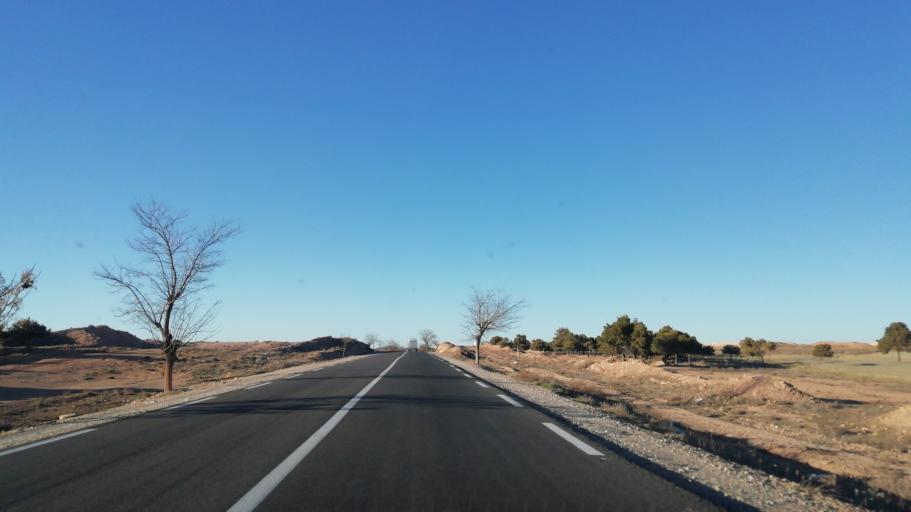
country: DZ
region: Tlemcen
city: Sebdou
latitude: 34.5297
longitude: -1.2946
